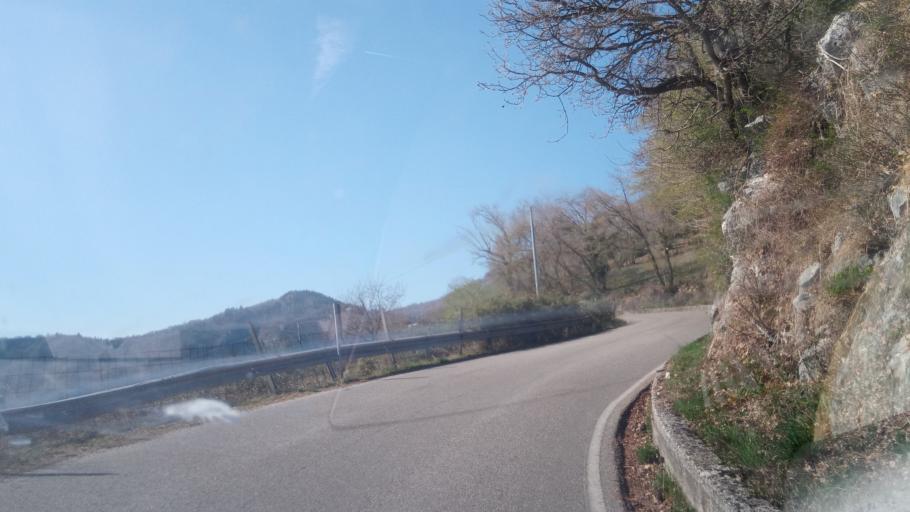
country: IT
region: Veneto
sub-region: Provincia di Treviso
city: Borso del Grappa
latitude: 45.8181
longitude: 11.7624
